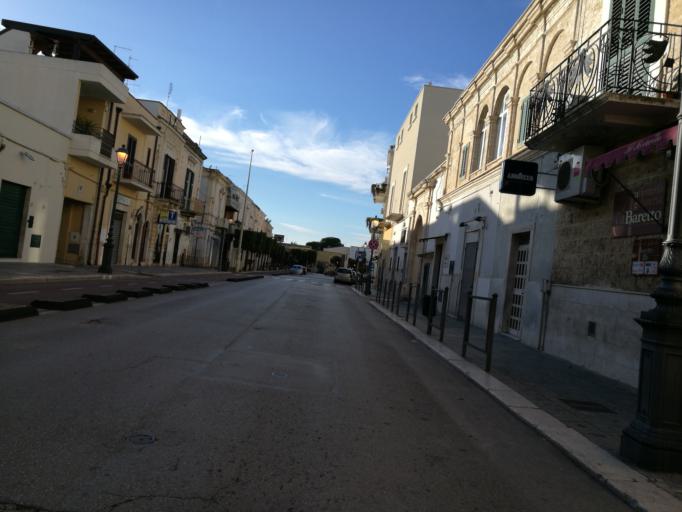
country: IT
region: Apulia
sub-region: Provincia di Bari
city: Adelfia
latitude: 41.0040
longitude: 16.8672
